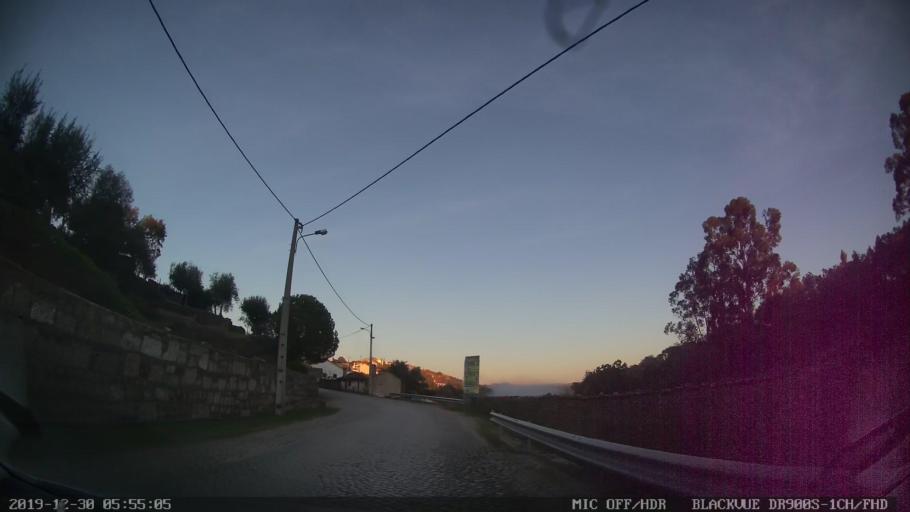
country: PT
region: Castelo Branco
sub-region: Idanha-A-Nova
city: Idanha-a-Nova
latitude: 40.0228
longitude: -7.2432
